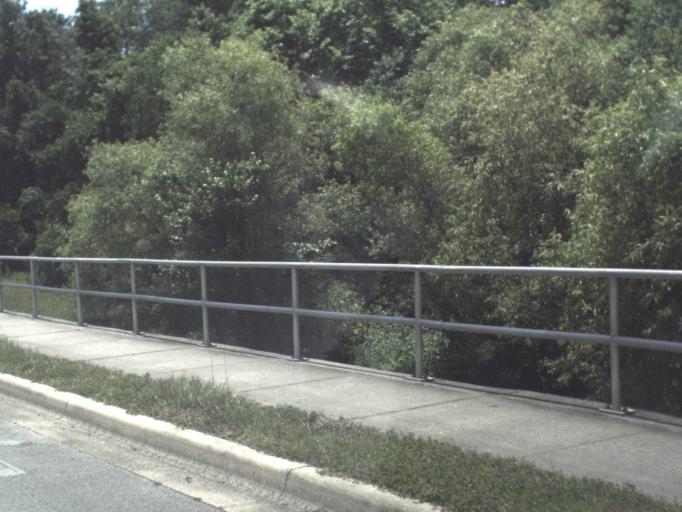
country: US
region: Florida
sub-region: Saint Johns County
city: Saint Augustine South
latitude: 29.8473
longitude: -81.3611
